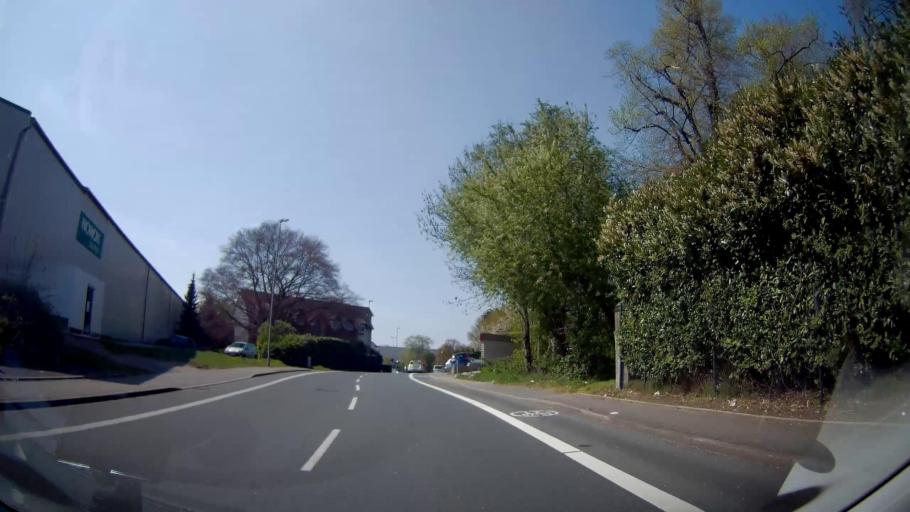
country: DE
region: North Rhine-Westphalia
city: Bochum-Hordel
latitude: 51.4858
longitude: 7.1602
